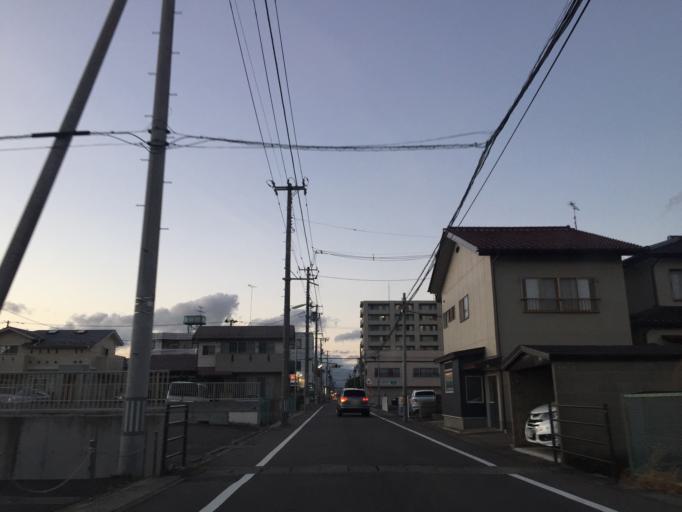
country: JP
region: Fukushima
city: Koriyama
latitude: 37.4009
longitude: 140.3561
